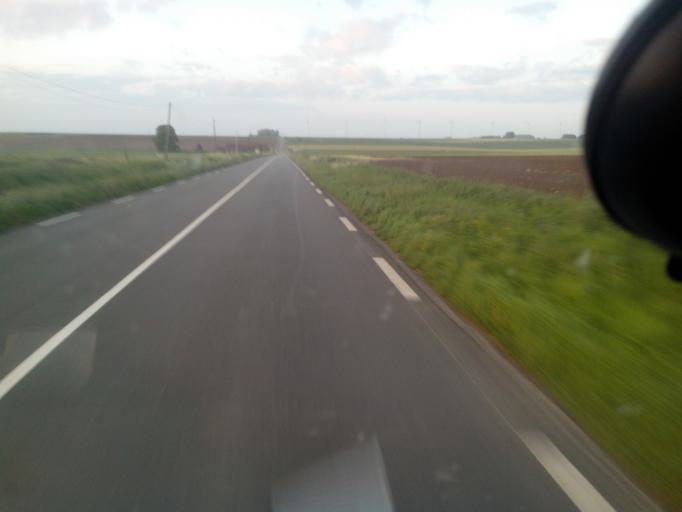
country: FR
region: Picardie
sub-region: Departement de la Somme
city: Crecy-en-Ponthieu
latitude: 50.2276
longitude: 1.9316
